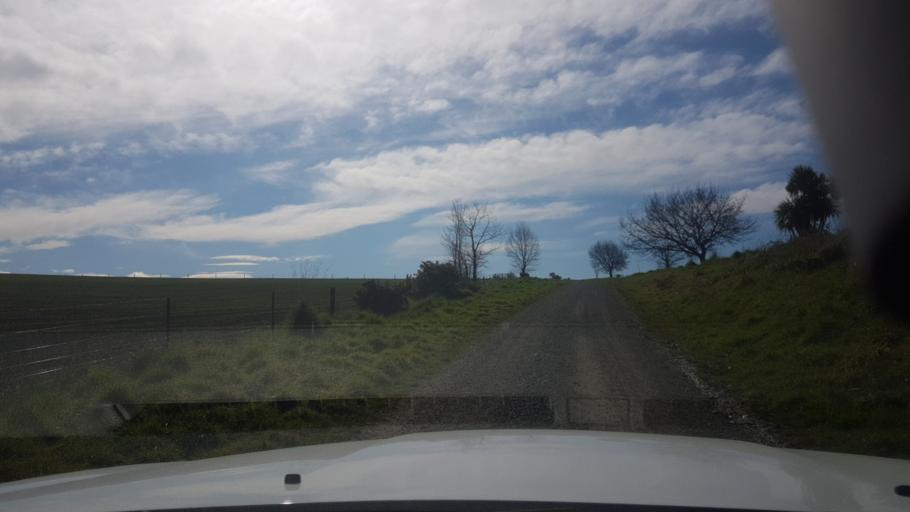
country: NZ
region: Canterbury
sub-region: Timaru District
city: Pleasant Point
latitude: -44.1998
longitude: 171.1872
